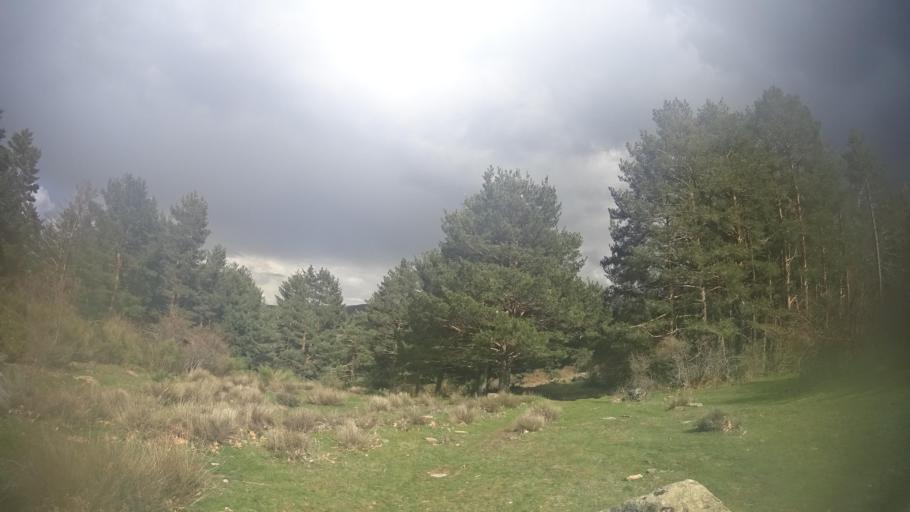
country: ES
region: Madrid
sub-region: Provincia de Madrid
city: Canencia
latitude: 40.8751
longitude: -3.7713
